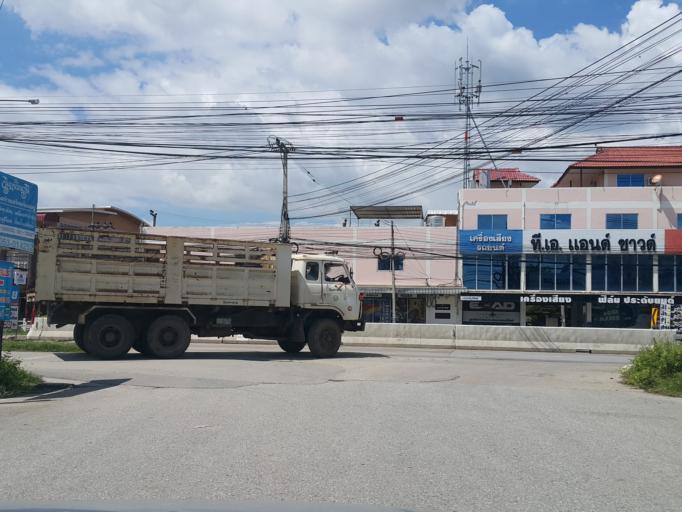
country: TH
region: Chiang Mai
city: Chiang Mai
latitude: 18.7407
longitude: 98.9646
